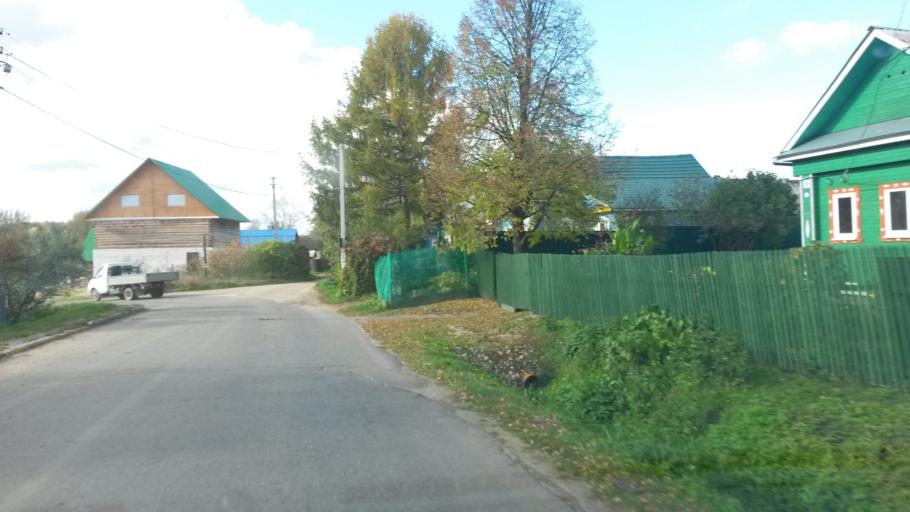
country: RU
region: Jaroslavl
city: Tunoshna
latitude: 57.5265
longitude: 39.9812
